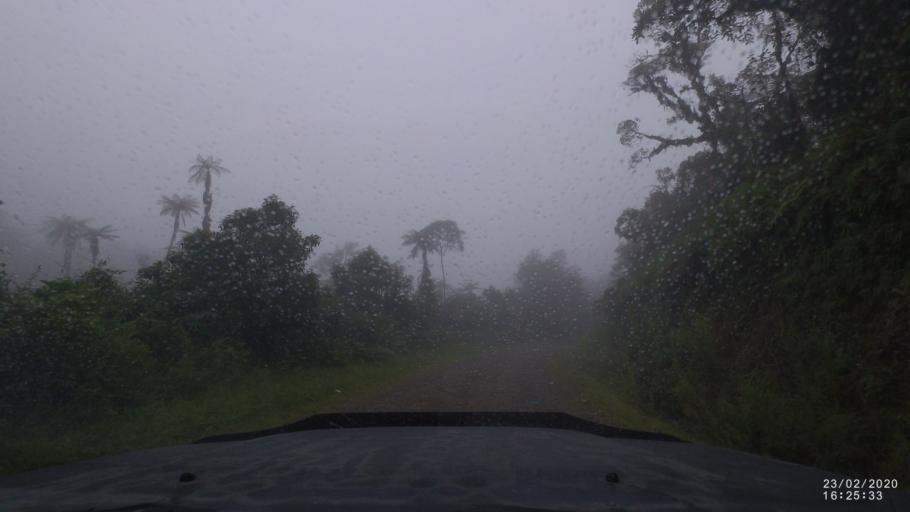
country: BO
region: Cochabamba
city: Colomi
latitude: -17.1035
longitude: -65.9794
